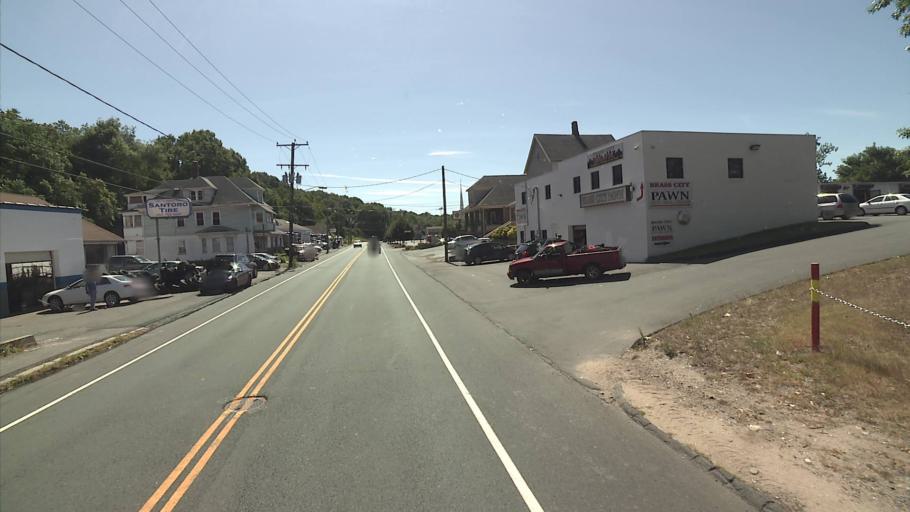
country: US
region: Connecticut
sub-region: New Haven County
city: Waterbury
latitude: 41.5834
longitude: -73.0488
